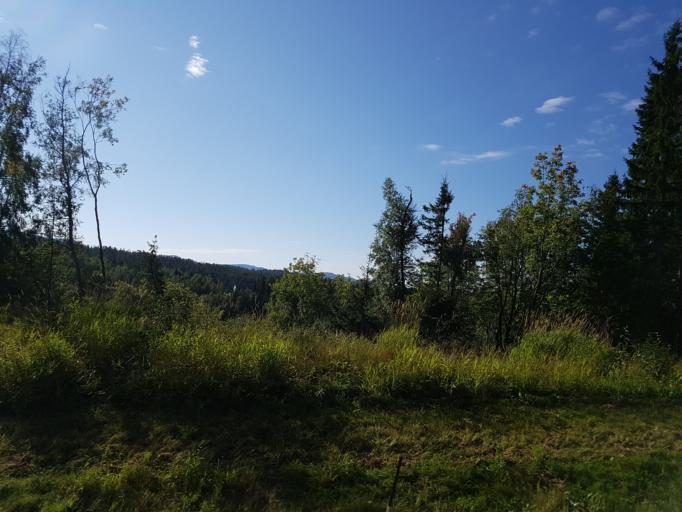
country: NO
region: Sor-Trondelag
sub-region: Trondheim
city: Trondheim
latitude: 63.6539
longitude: 10.2518
